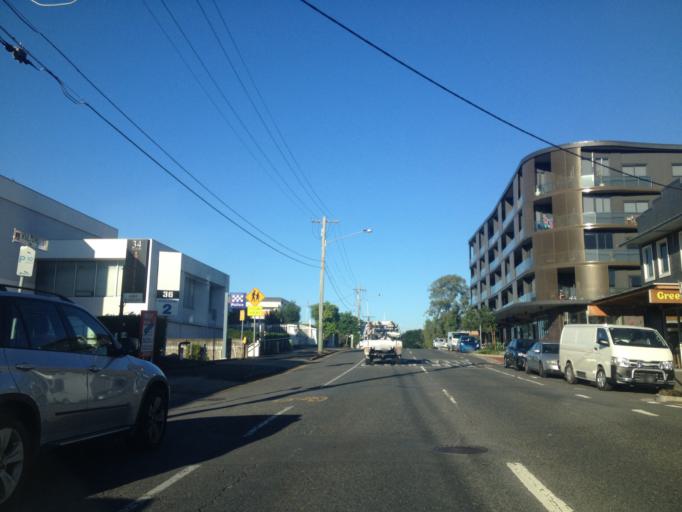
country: AU
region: Queensland
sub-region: Brisbane
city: Milton
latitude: -27.4804
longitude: 153.0089
